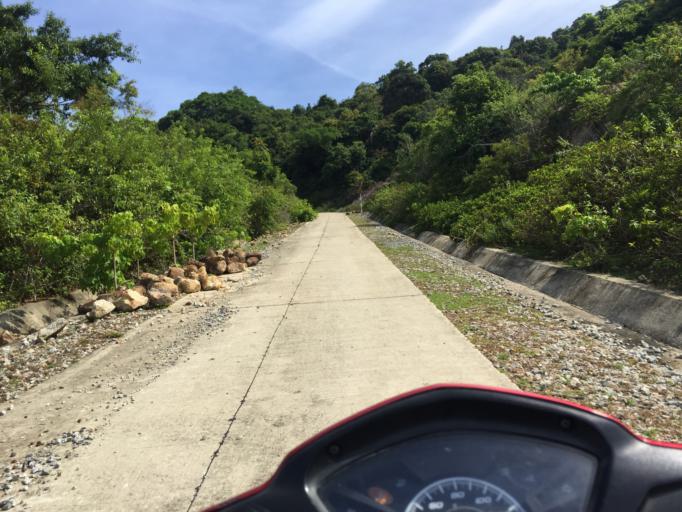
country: VN
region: Quang Nam
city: Hoi An
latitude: 15.9377
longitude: 108.5331
